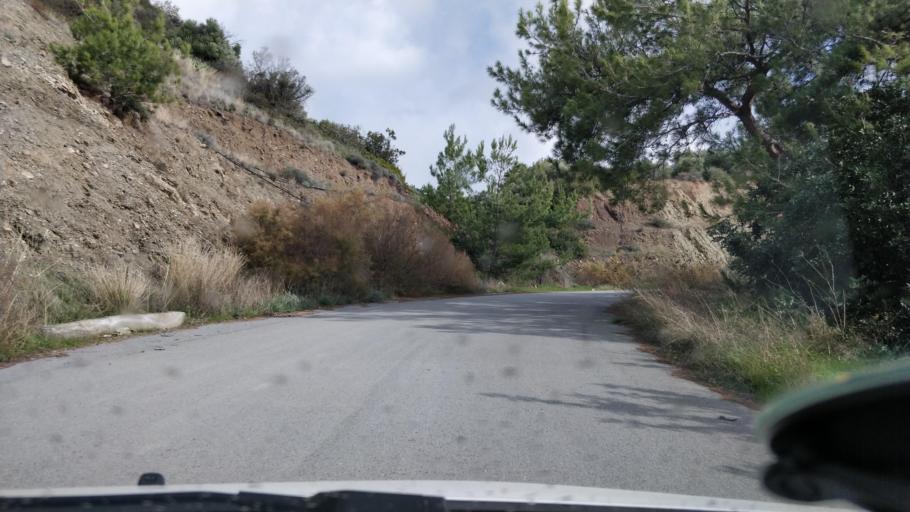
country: GR
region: Crete
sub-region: Nomos Lasithiou
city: Gra Liyia
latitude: 34.9955
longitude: 25.5109
